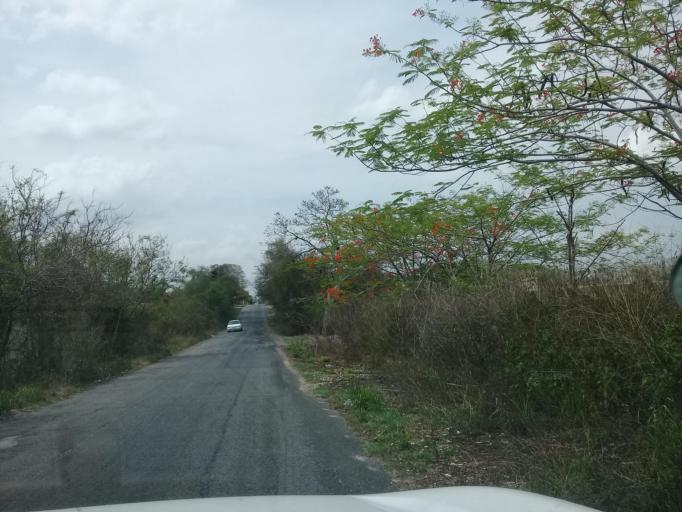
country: MX
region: Veracruz
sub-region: Emiliano Zapata
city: Plan del Rio
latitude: 19.3534
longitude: -96.6586
